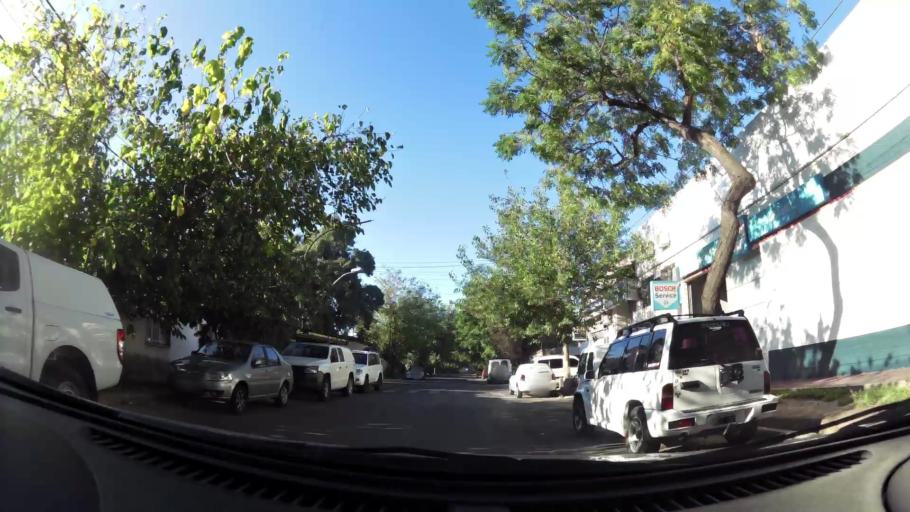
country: AR
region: Mendoza
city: Mendoza
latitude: -32.8725
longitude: -68.8234
